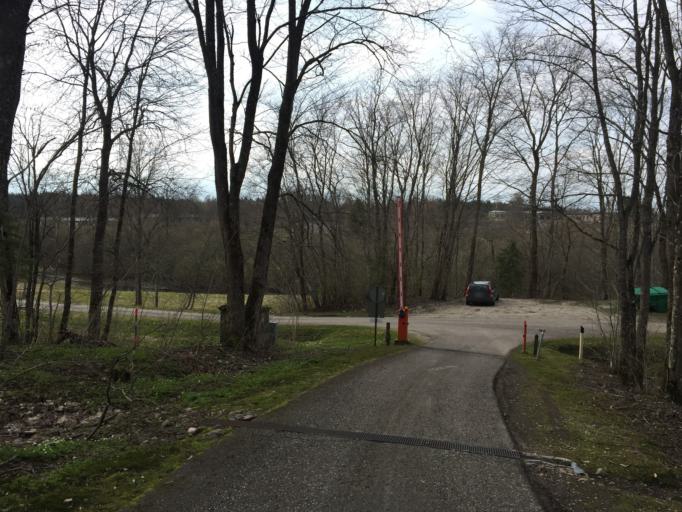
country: EE
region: Vorumaa
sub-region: Voru linn
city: Voru
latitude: 57.7170
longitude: 27.0572
